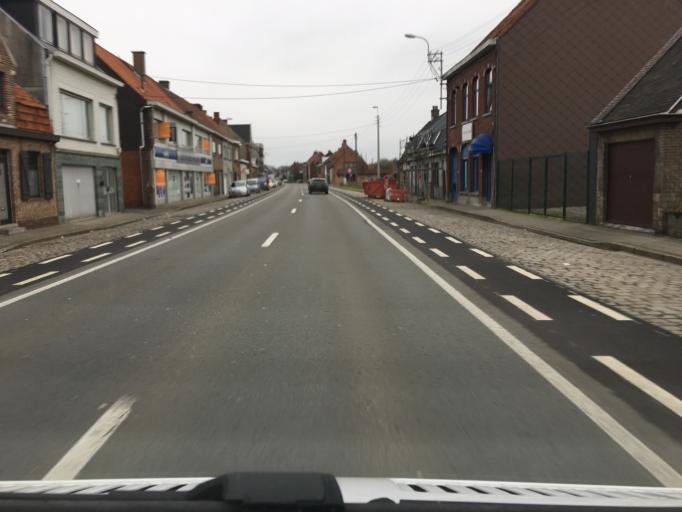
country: BE
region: Flanders
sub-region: Provincie West-Vlaanderen
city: Wevelgem
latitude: 50.8047
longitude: 3.1676
